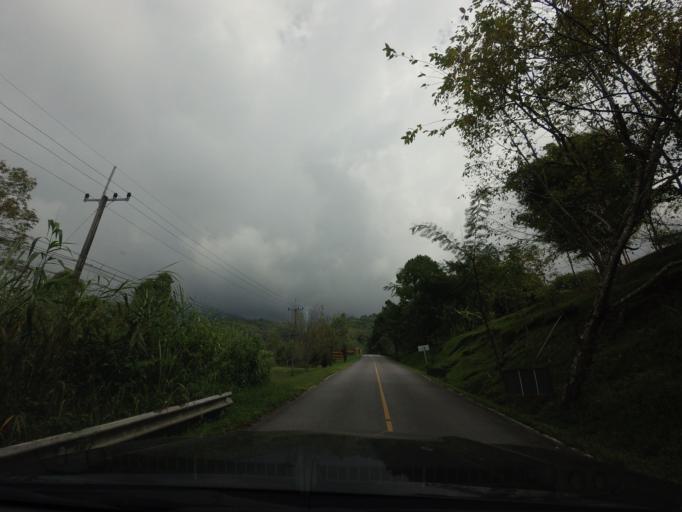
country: TH
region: Nan
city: Bo Kluea
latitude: 19.2074
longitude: 101.0718
